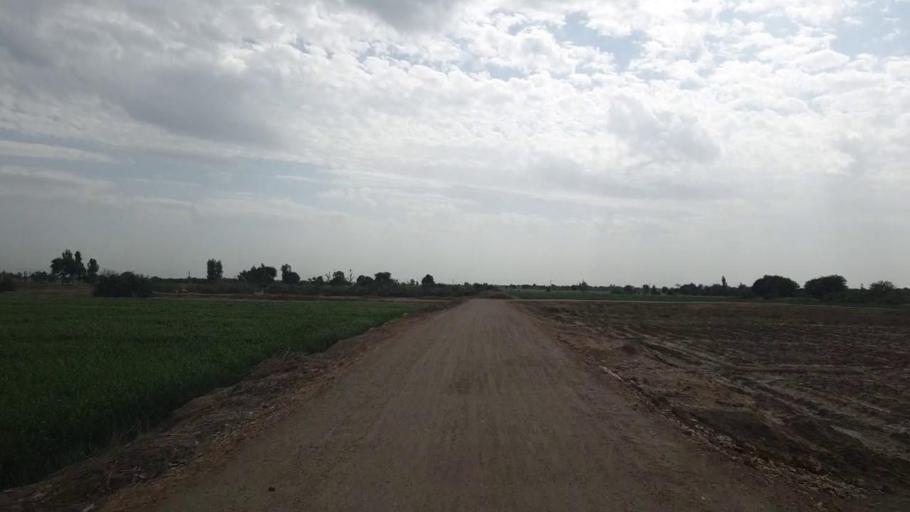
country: PK
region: Sindh
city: Hala
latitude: 25.9261
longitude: 68.4338
